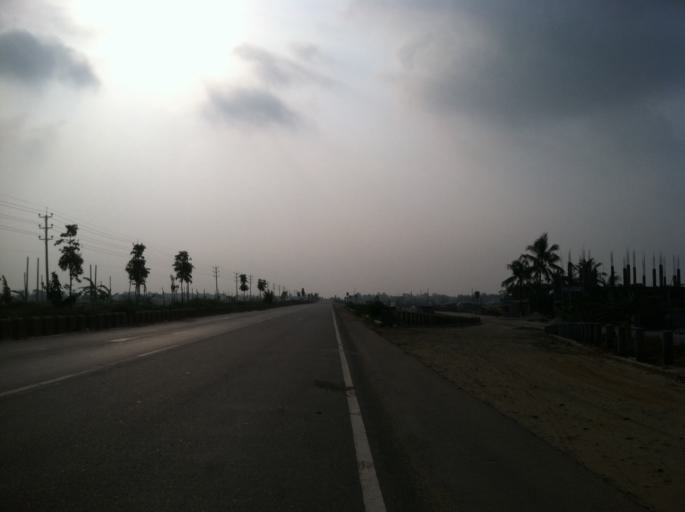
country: BD
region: Dhaka
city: Tungi
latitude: 23.8373
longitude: 90.4815
